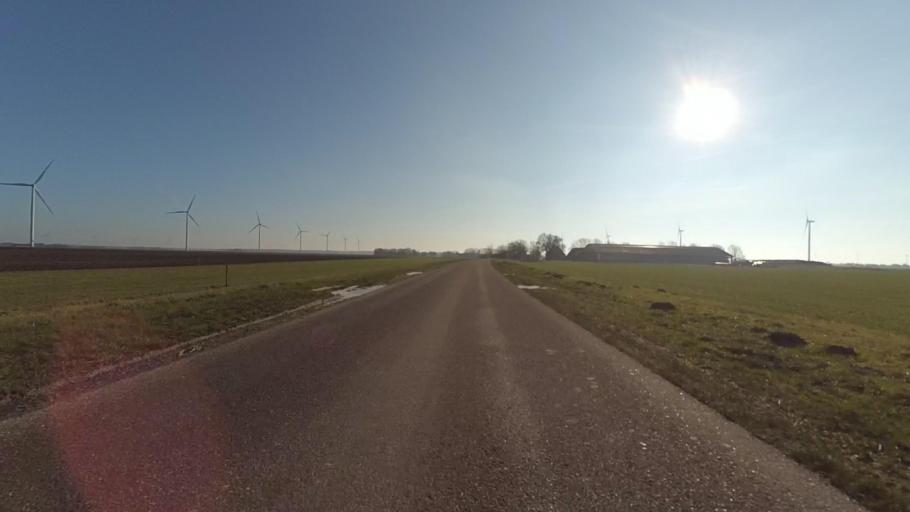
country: NL
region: Utrecht
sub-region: Gemeente Bunschoten
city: Spakenburg
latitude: 52.2989
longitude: 5.3857
